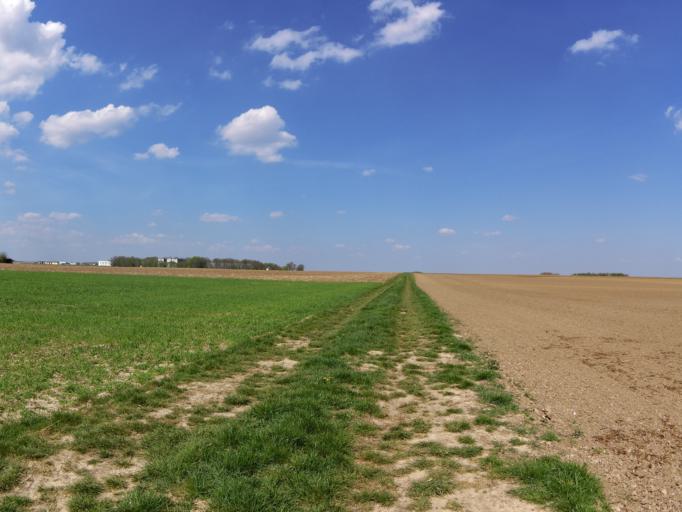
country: DE
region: Bavaria
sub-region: Regierungsbezirk Unterfranken
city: Giebelstadt
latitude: 49.6792
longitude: 9.9563
